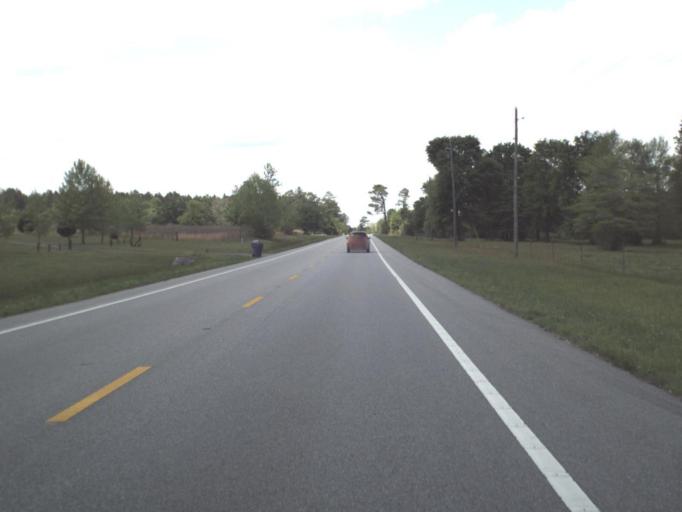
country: US
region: Florida
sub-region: Escambia County
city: Molino
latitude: 30.7820
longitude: -87.4035
